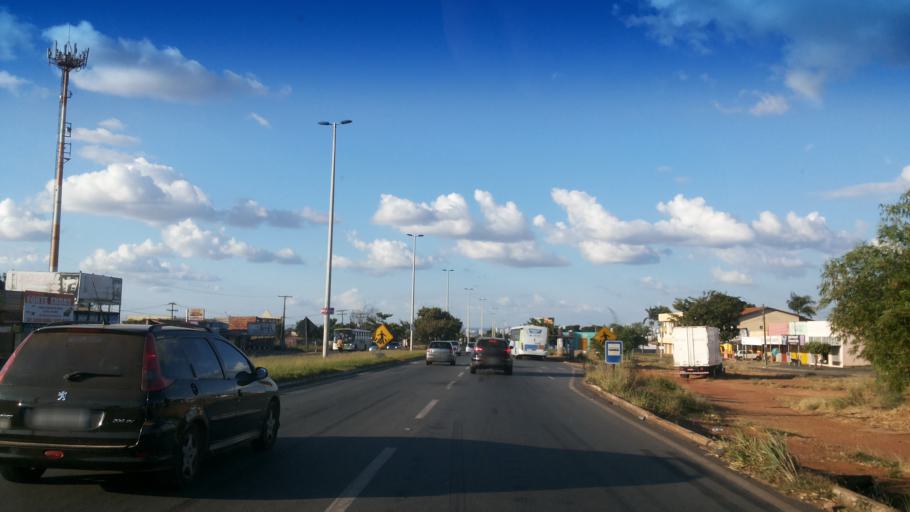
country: BR
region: Goias
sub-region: Goiania
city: Goiania
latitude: -16.7520
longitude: -49.3353
